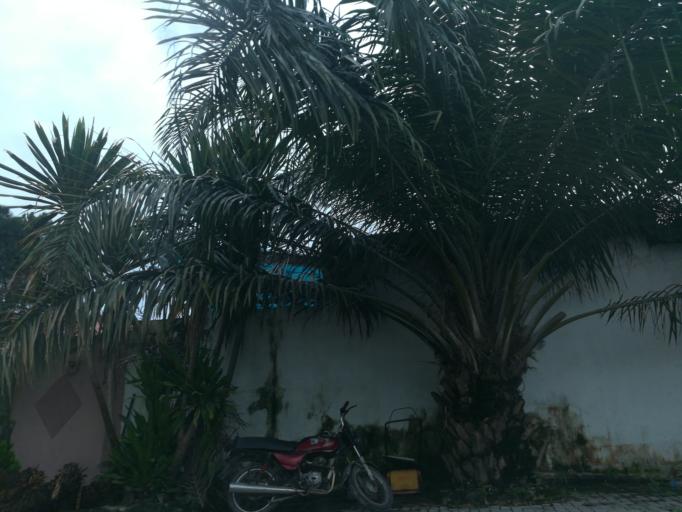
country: NG
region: Lagos
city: Ikoyi
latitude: 6.4375
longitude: 3.4749
